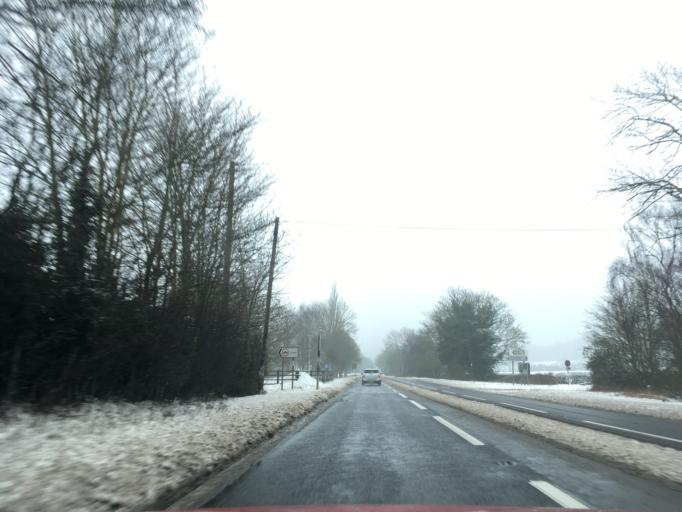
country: GB
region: England
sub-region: Warwickshire
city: Alcester
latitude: 52.2072
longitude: -1.8246
